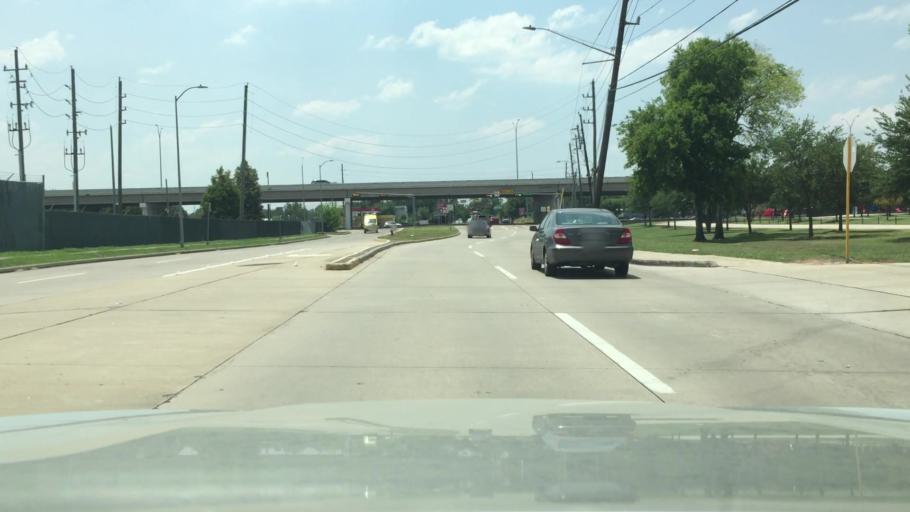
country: US
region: Texas
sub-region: Fort Bend County
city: Meadows Place
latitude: 29.7170
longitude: -95.5923
